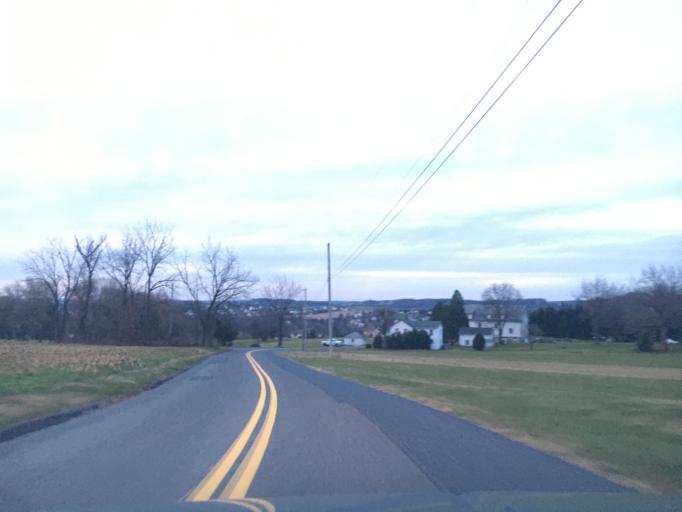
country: US
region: Pennsylvania
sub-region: Lehigh County
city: Schnecksville
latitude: 40.6926
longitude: -75.5769
